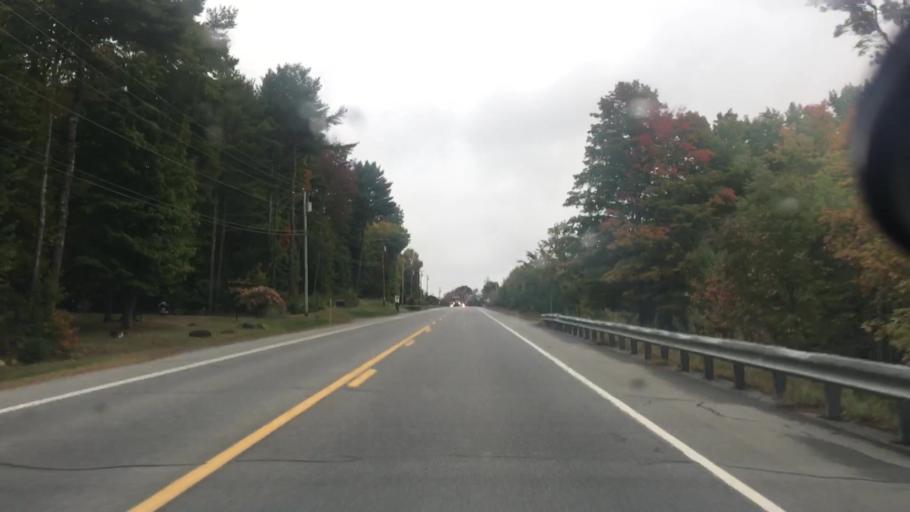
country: US
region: Maine
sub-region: Kennebec County
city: Belgrade
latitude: 44.3998
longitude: -69.8076
